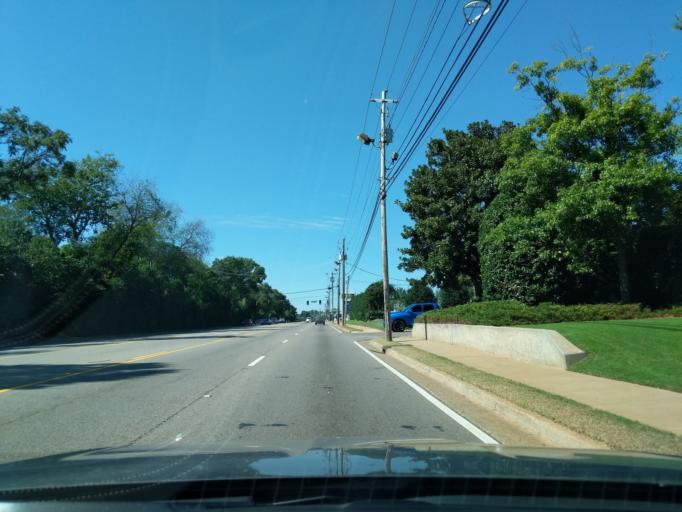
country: US
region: South Carolina
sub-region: Aiken County
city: North Augusta
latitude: 33.5057
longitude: -82.0179
